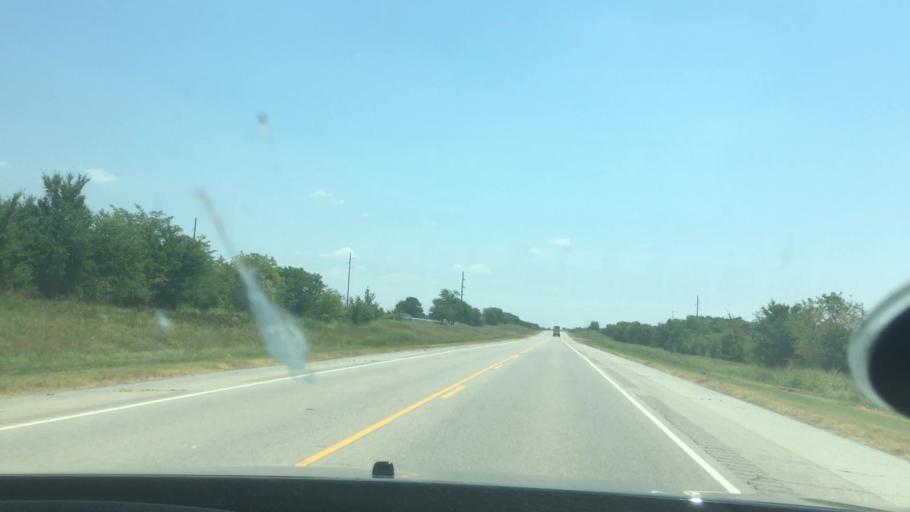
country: US
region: Oklahoma
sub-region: Pontotoc County
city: Ada
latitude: 34.6375
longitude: -96.4804
